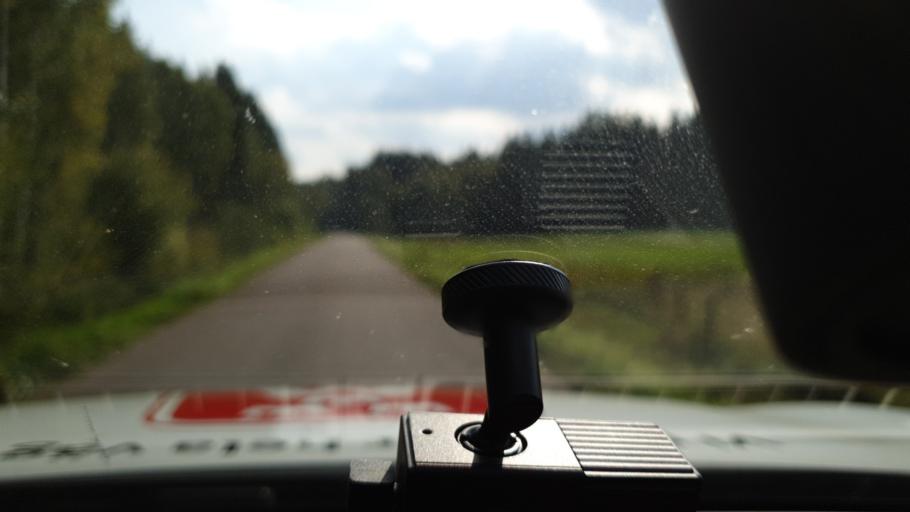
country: SE
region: Kalmar
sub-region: Vimmerby Kommun
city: Sodra Vi
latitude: 57.8408
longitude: 15.8438
